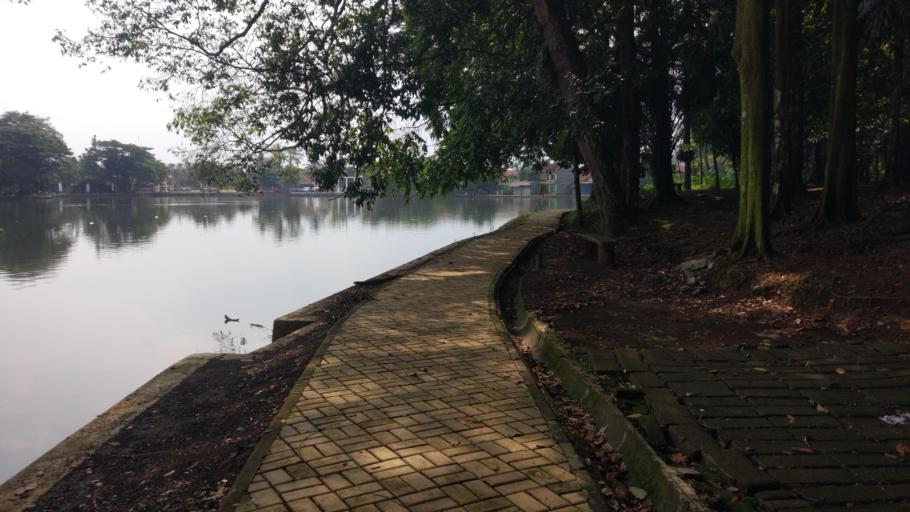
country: ID
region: West Java
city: Ciampea
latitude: -6.5524
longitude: 106.7476
